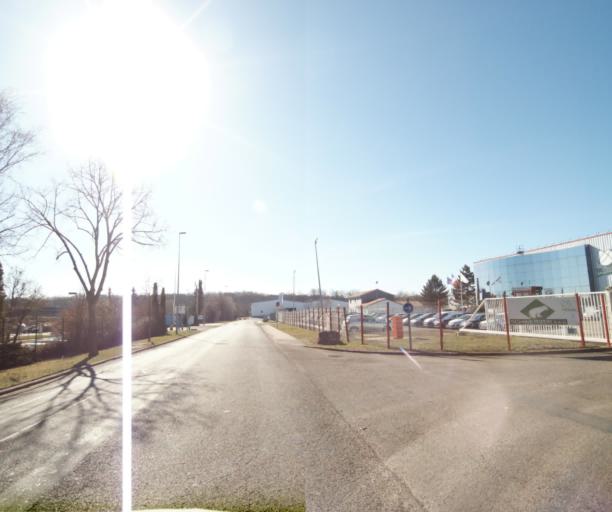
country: FR
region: Lorraine
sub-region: Departement de Meurthe-et-Moselle
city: Richardmenil
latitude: 48.6109
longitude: 6.1858
